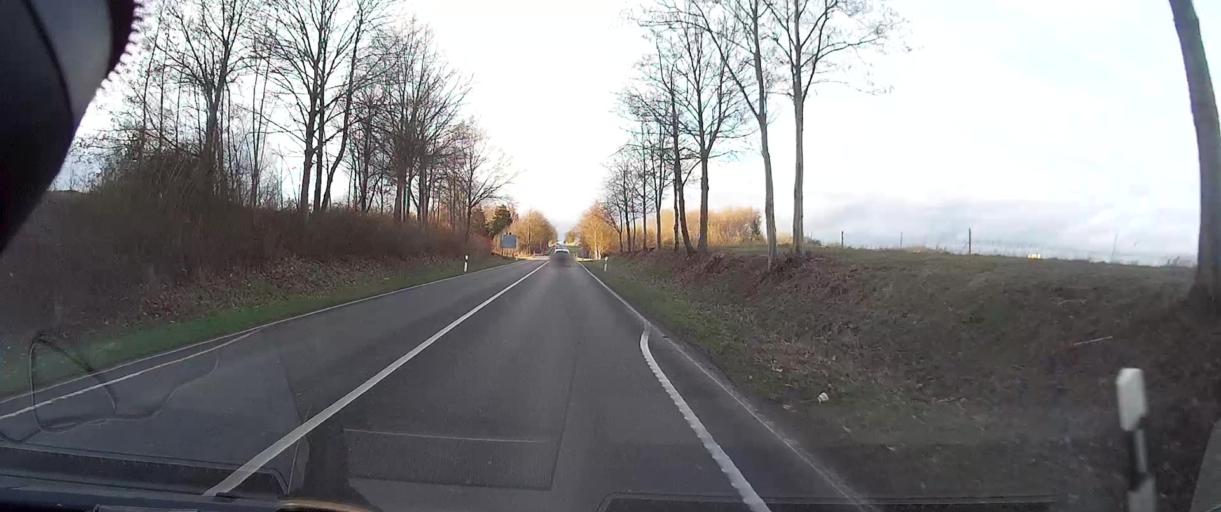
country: DE
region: Rheinland-Pfalz
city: Wirges
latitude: 50.4591
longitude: 7.8044
